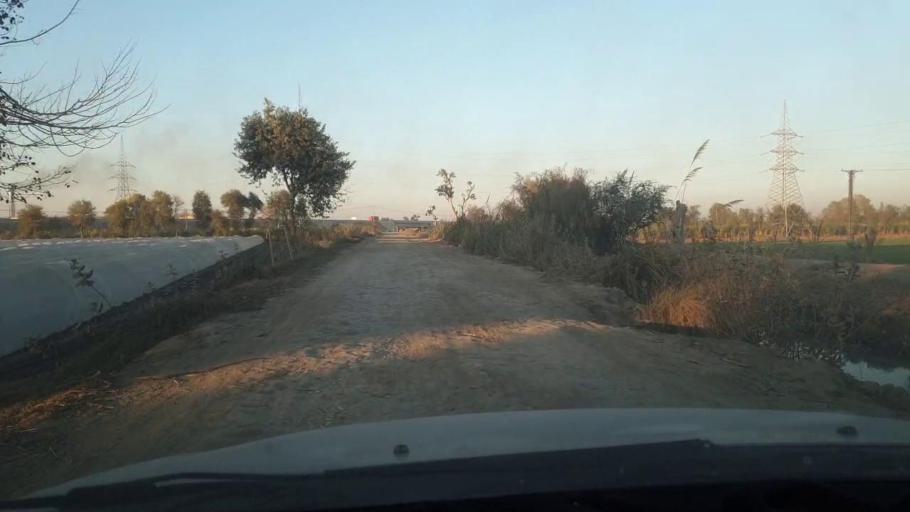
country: PK
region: Sindh
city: Ghotki
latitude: 28.0412
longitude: 69.3246
